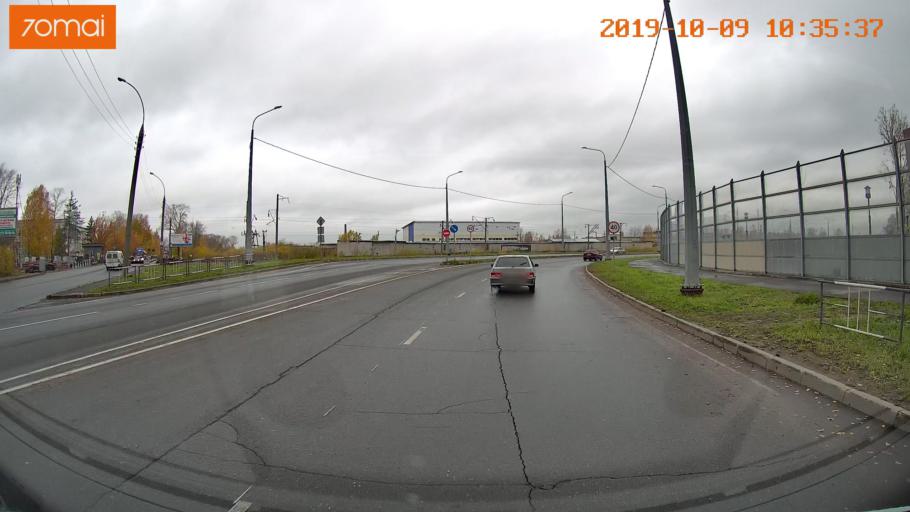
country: RU
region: Vologda
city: Vologda
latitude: 59.2270
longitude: 39.8619
